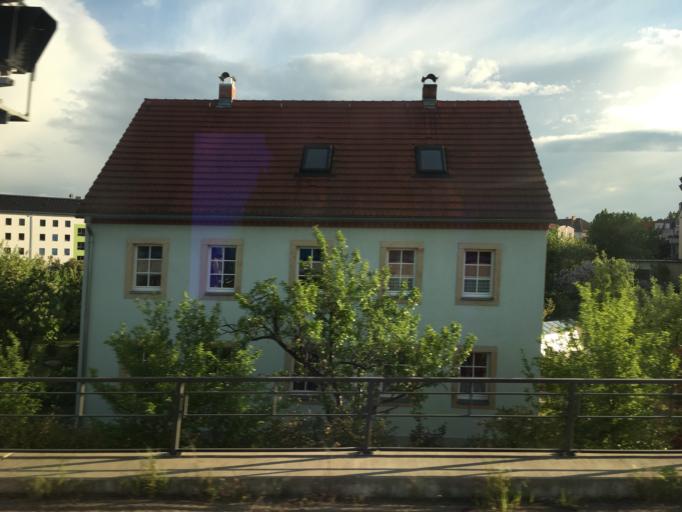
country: DE
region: Saxony
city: Dresden
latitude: 51.0867
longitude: 13.7156
